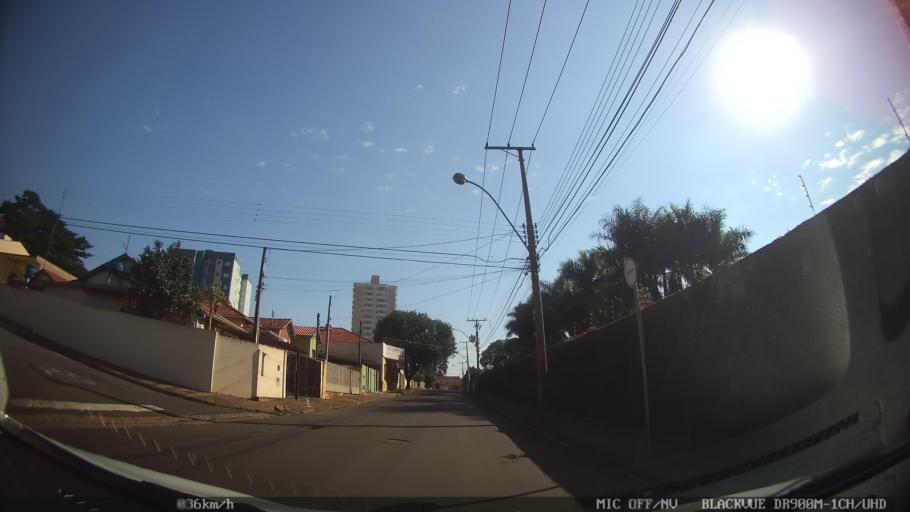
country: BR
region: Sao Paulo
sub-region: Americana
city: Americana
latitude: -22.7471
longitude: -47.3229
